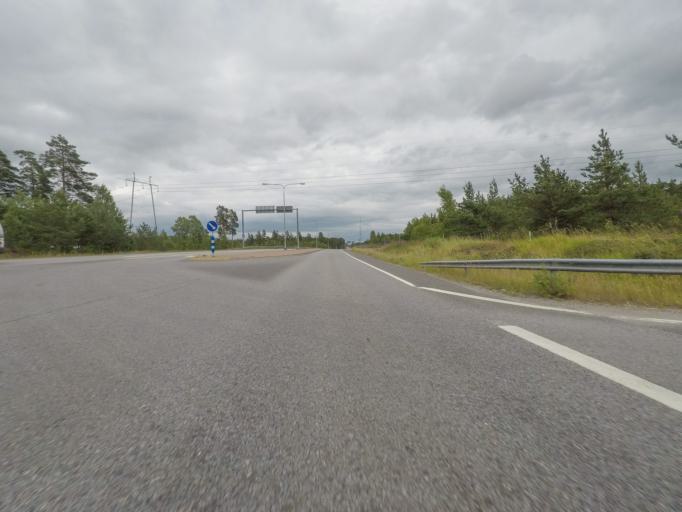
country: FI
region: Varsinais-Suomi
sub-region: Turku
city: Piikkioe
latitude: 60.4436
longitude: 22.4889
